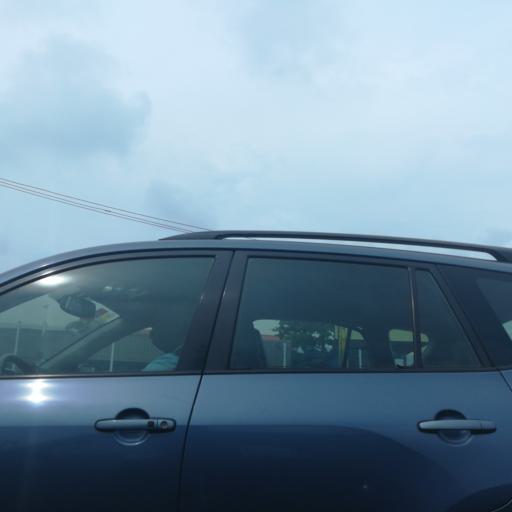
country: NG
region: Lagos
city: Ojota
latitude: 6.5844
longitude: 3.3903
